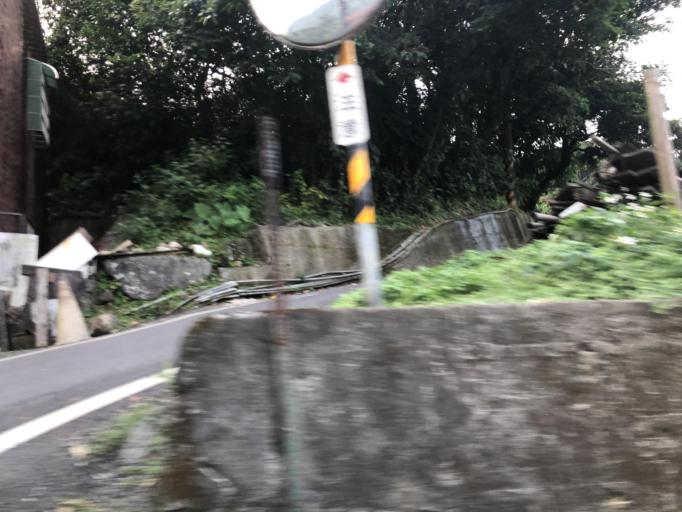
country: TW
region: Taiwan
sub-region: Keelung
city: Keelung
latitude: 25.1953
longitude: 121.6443
